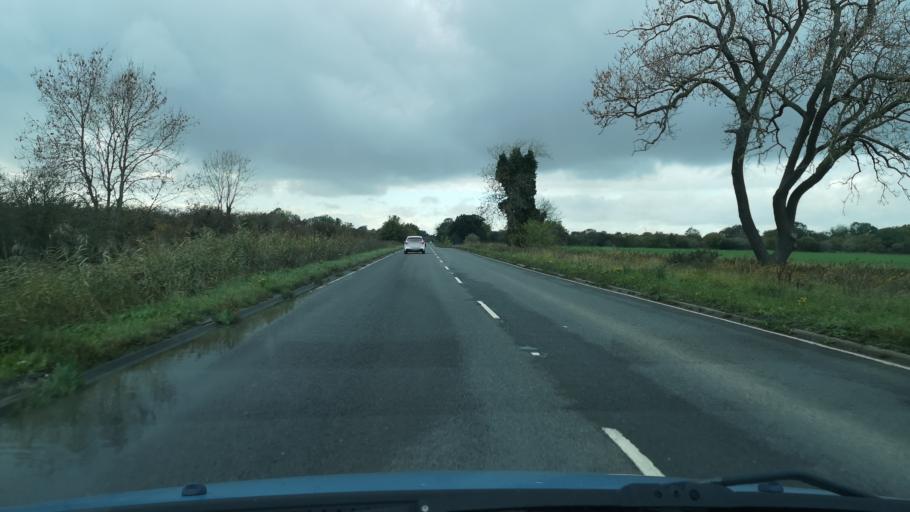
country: GB
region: England
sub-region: North Lincolnshire
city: Belton
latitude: 53.5821
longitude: -0.8013
